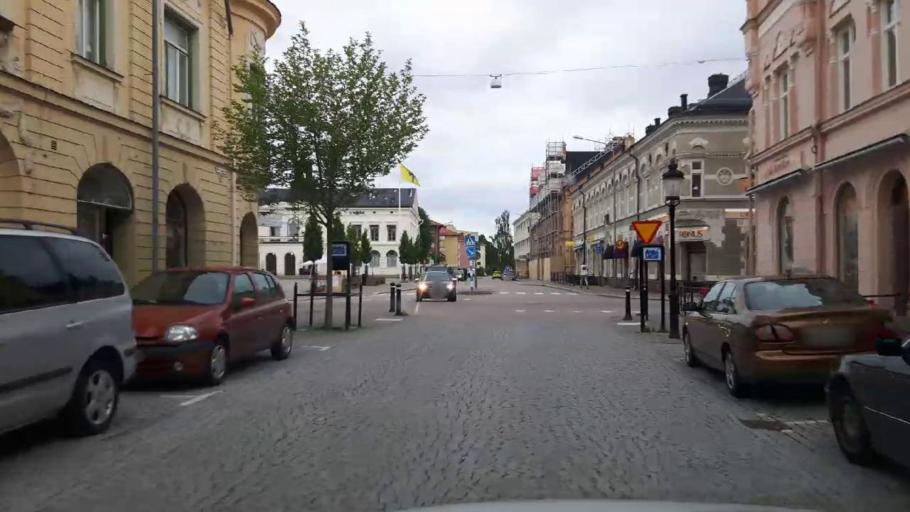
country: SE
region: Vaestmanland
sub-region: Kopings Kommun
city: Koping
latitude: 59.5134
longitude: 15.9939
